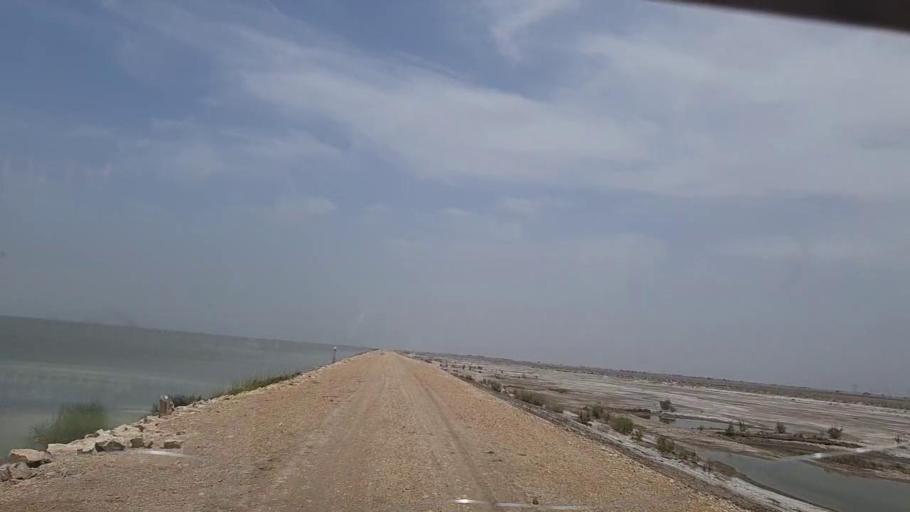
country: PK
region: Sindh
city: Sehwan
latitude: 26.4119
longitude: 67.7884
